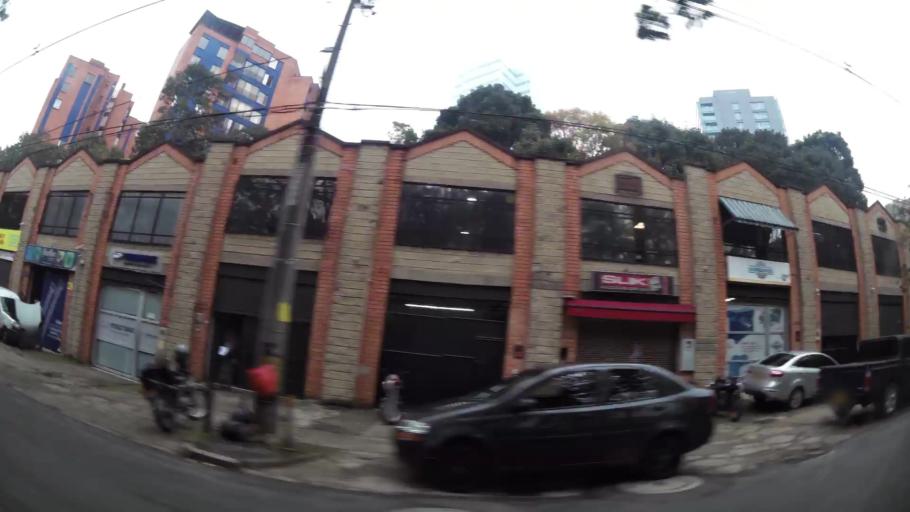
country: CO
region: Antioquia
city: Medellin
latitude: 6.2181
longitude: -75.5718
